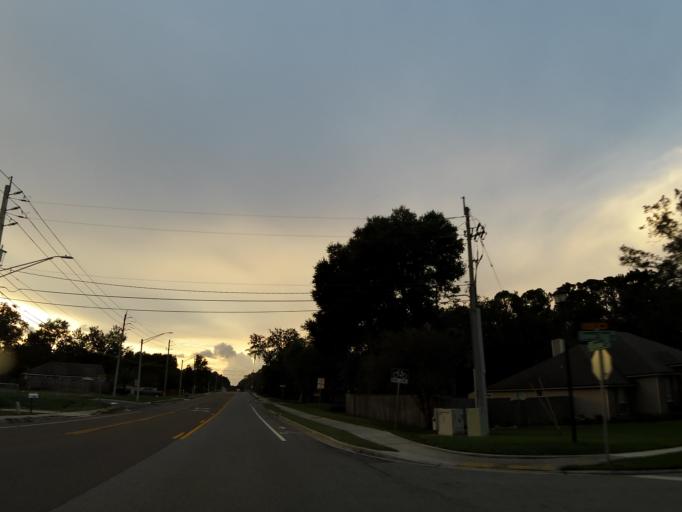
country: US
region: Florida
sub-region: Duval County
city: Jacksonville
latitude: 30.3599
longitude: -81.5509
